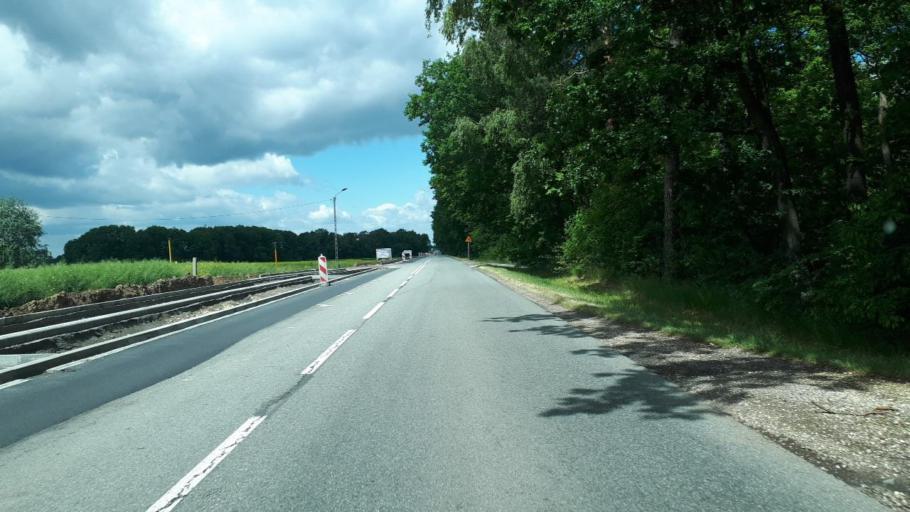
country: PL
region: Silesian Voivodeship
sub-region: Powiat pszczynski
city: Miedzna
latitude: 49.9704
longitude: 19.0217
